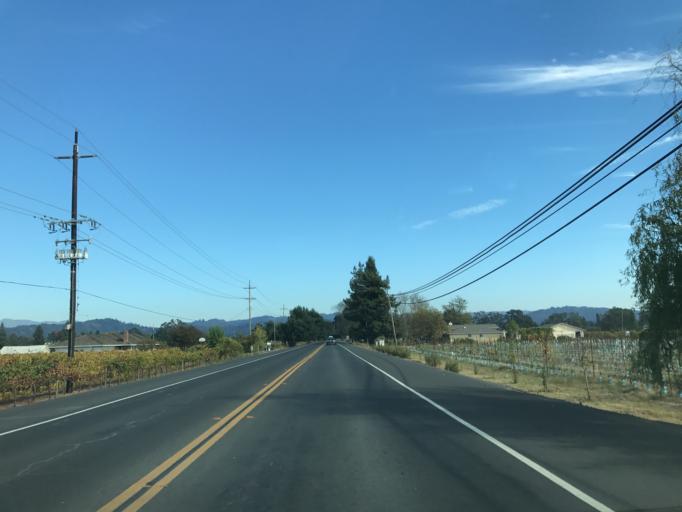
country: US
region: California
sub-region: Sonoma County
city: Larkfield-Wikiup
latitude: 38.4945
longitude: -122.7842
